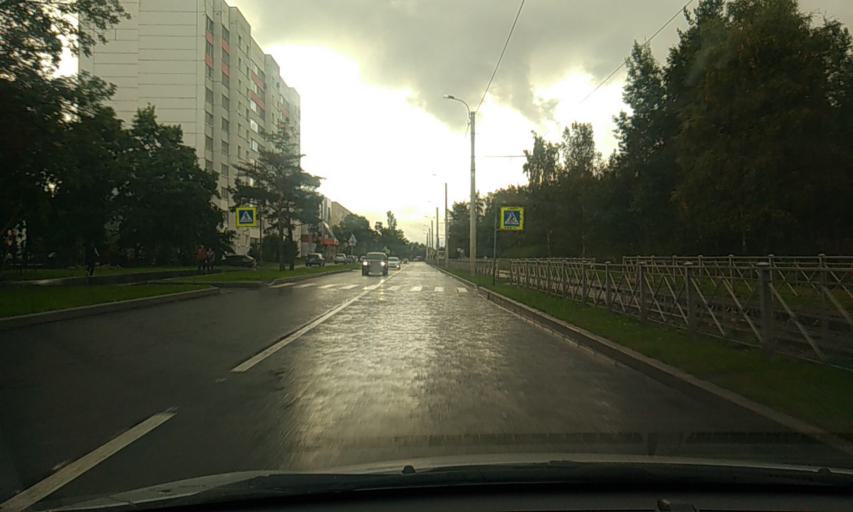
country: RU
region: St.-Petersburg
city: Sosnovaya Polyana
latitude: 59.8285
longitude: 30.1403
